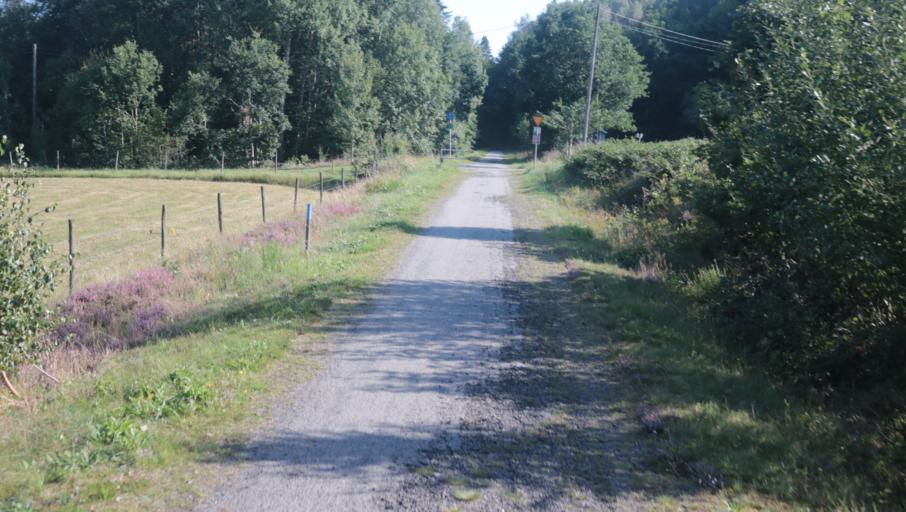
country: SE
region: Blekinge
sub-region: Karlshamns Kommun
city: Svangsta
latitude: 56.2713
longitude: 14.7619
